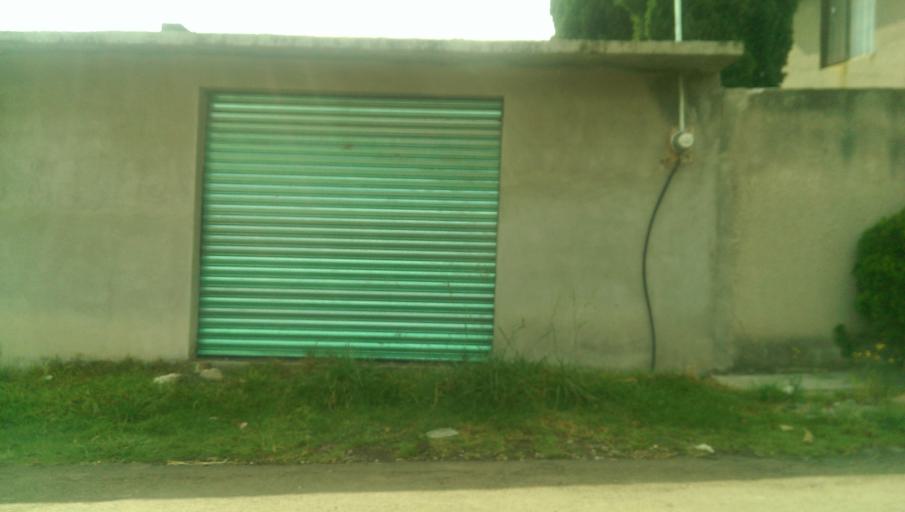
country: MX
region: Mexico
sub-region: Jilotepec
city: Jilotepec de Molina Enriquez
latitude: 19.9490
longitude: -99.4892
